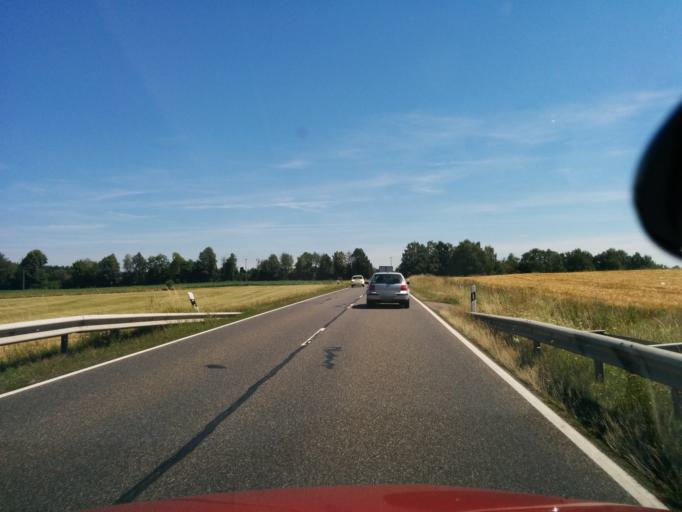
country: DE
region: Rheinland-Pfalz
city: Ailertchen
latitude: 50.5958
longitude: 7.9338
